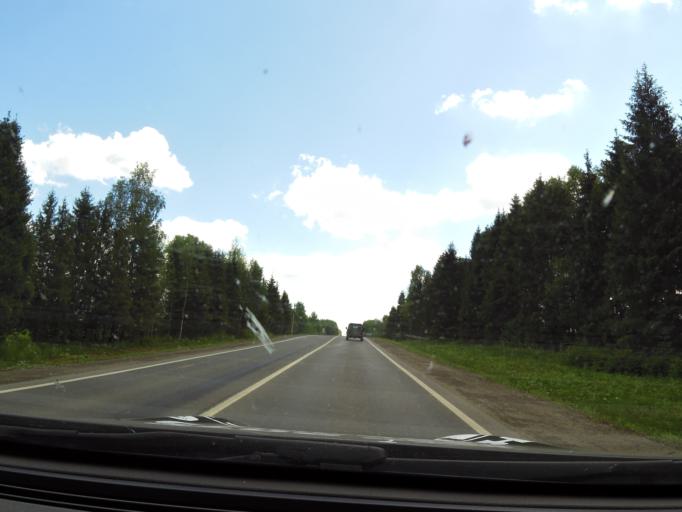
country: RU
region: Vologda
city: Molochnoye
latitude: 59.2644
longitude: 39.7404
